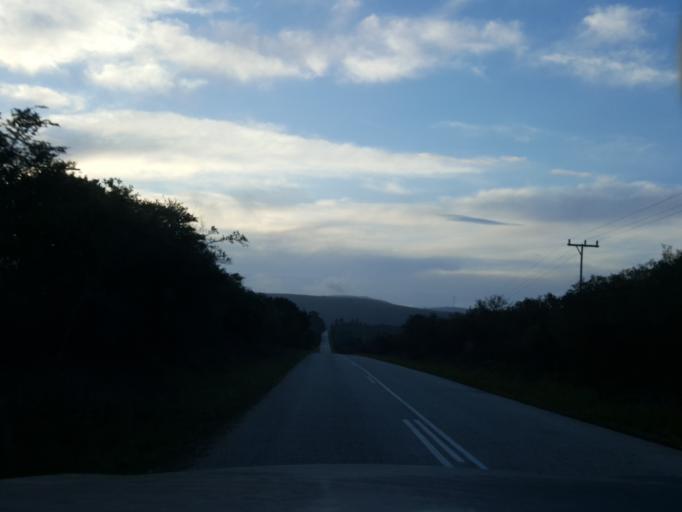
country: ZA
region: Eastern Cape
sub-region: Cacadu District Municipality
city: Grahamstown
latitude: -33.3902
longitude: 26.4744
